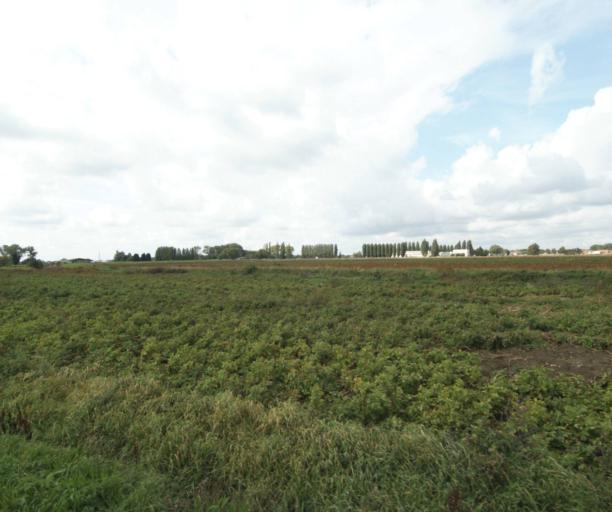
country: FR
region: Nord-Pas-de-Calais
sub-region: Departement du Nord
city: Houplines
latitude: 50.6871
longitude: 2.9269
